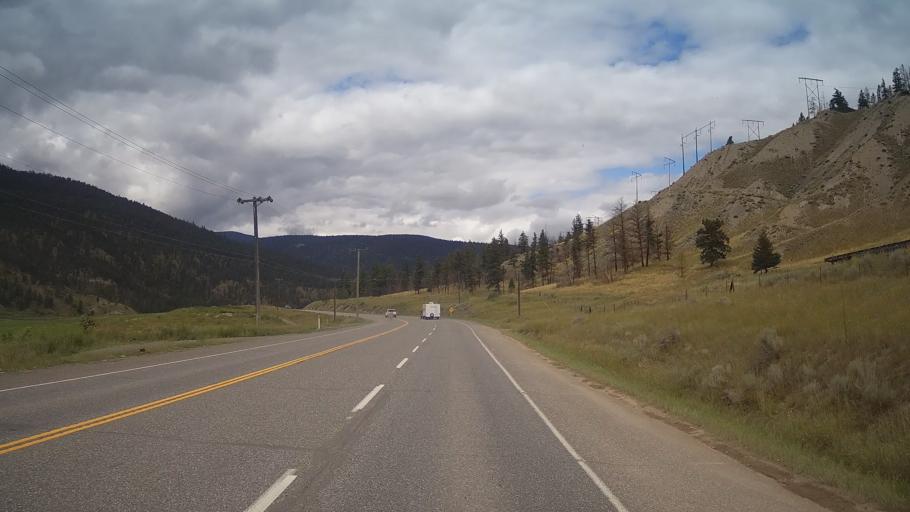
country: CA
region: British Columbia
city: Cache Creek
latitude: 50.9786
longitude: -121.4960
